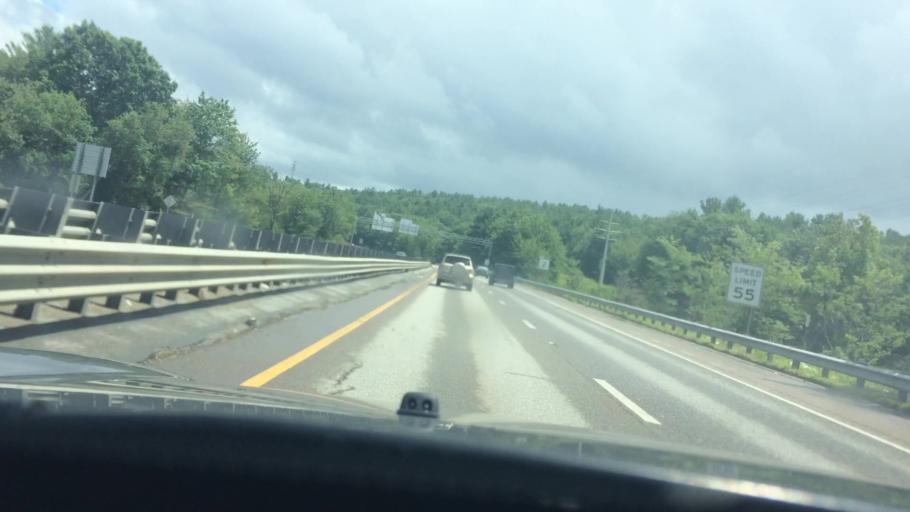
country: US
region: Massachusetts
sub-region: Worcester County
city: Fitchburg
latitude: 42.5493
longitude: -71.8453
